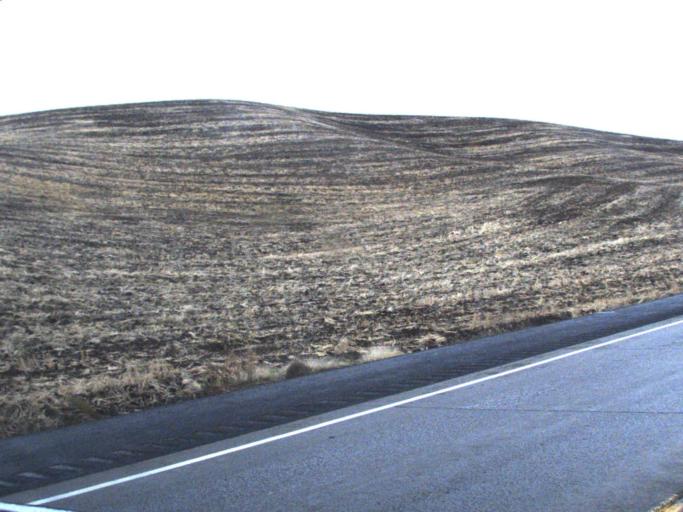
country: US
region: Washington
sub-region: Whitman County
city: Colfax
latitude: 46.9777
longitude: -117.3332
